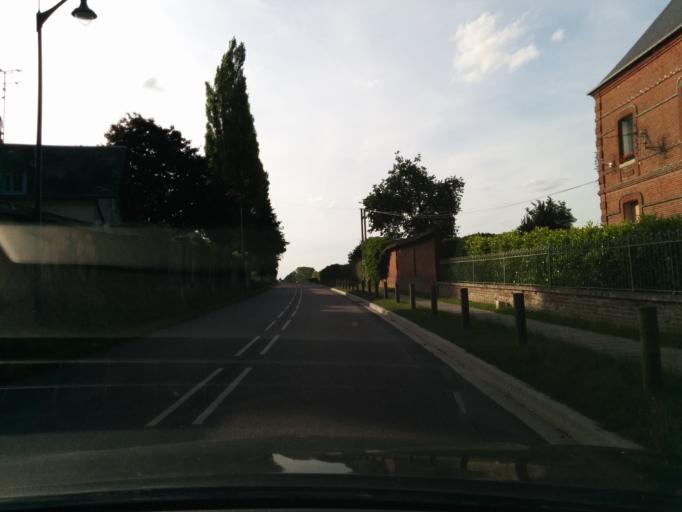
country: FR
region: Haute-Normandie
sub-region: Departement de la Seine-Maritime
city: La Feuillie
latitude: 49.4657
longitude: 1.5157
